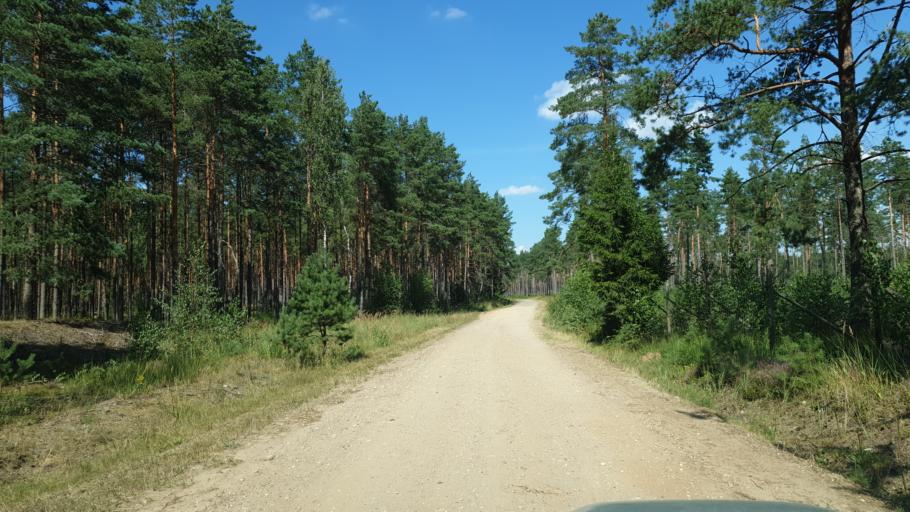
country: LT
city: Sirvintos
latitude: 54.8955
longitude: 24.9572
